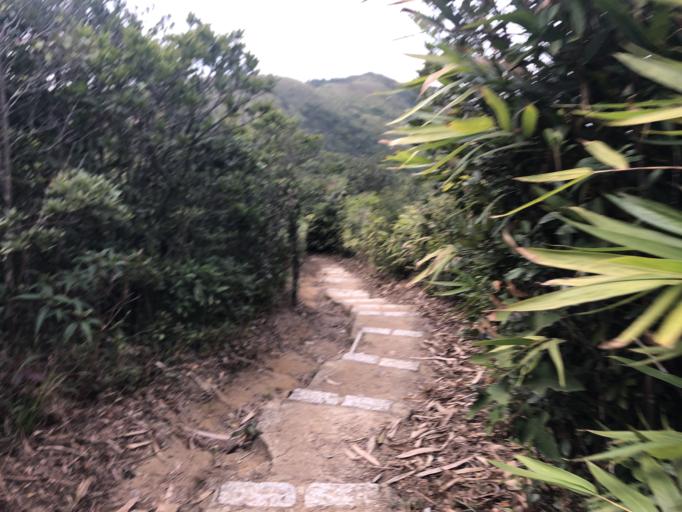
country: HK
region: Wanchai
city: Wan Chai
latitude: 22.2685
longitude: 114.2100
